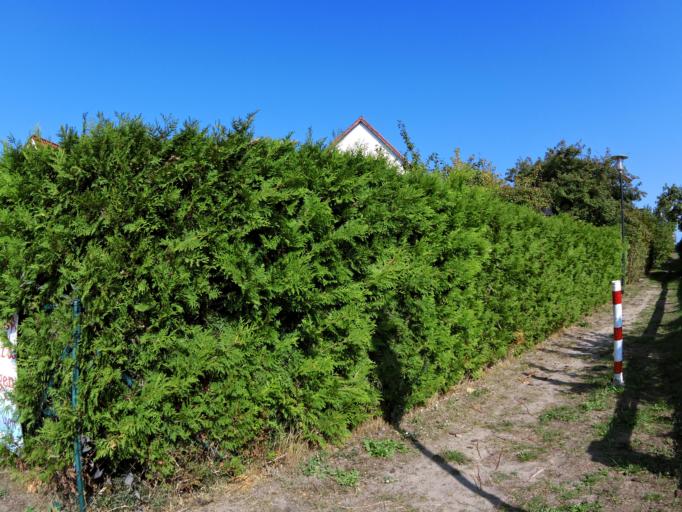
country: DE
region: Mecklenburg-Vorpommern
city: Loddin
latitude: 54.0133
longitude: 14.0427
